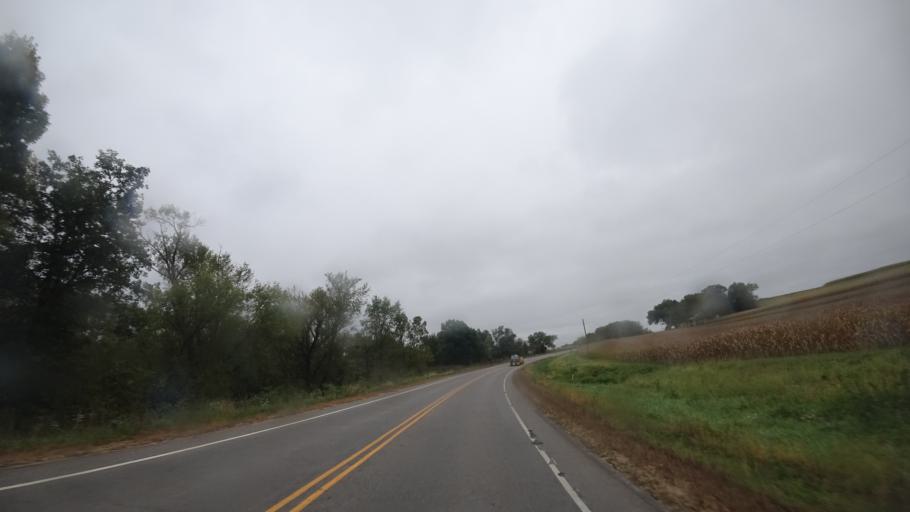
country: US
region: Wisconsin
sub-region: Crawford County
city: Prairie du Chien
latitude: 43.0335
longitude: -90.9896
